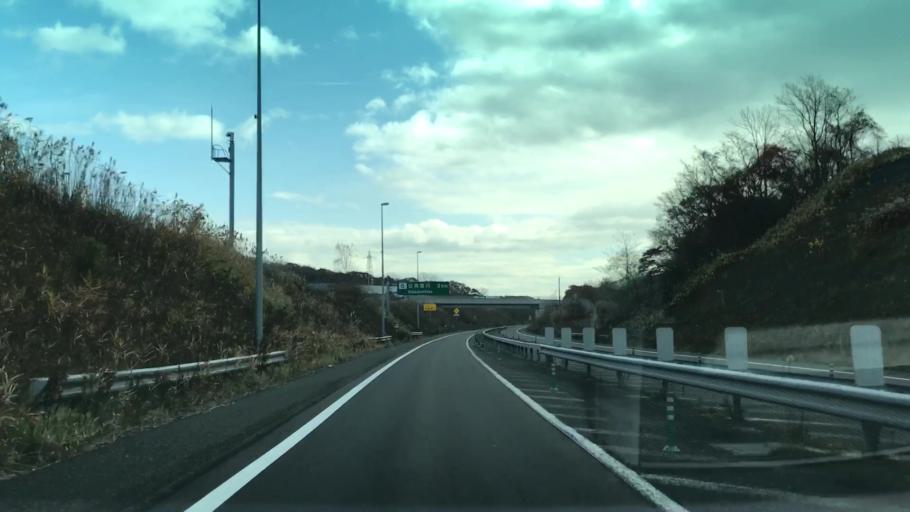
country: JP
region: Hokkaido
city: Shizunai-furukawacho
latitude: 42.5414
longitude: 142.0145
